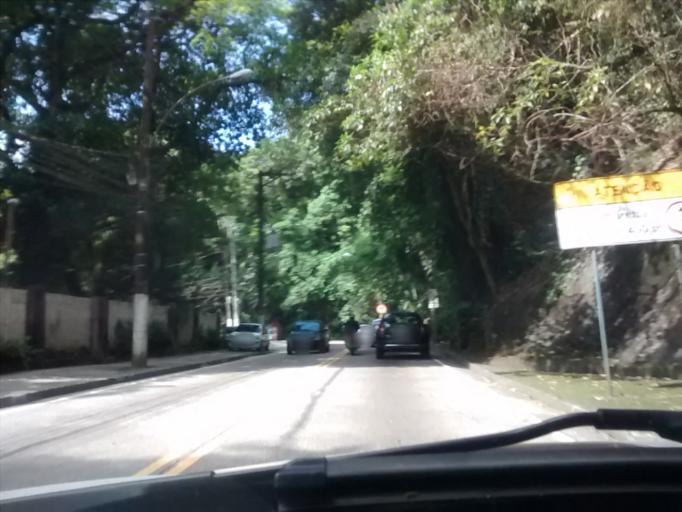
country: BR
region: Rio de Janeiro
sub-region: Rio De Janeiro
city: Rio de Janeiro
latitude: -22.9690
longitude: -43.2790
